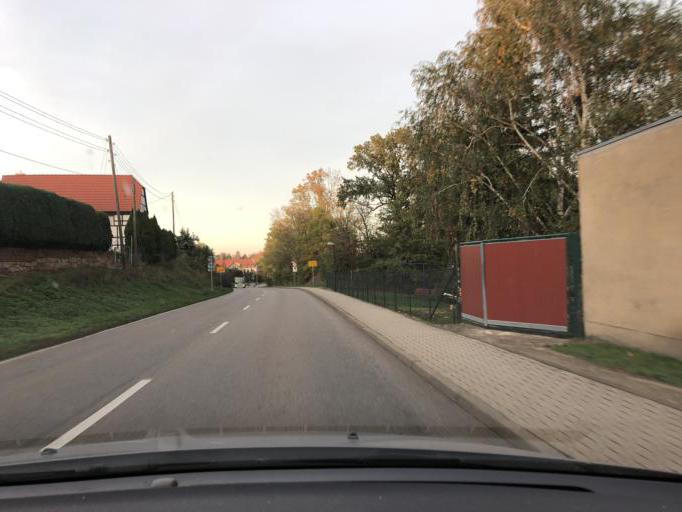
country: DE
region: Saxony
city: Elstertrebnitz
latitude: 51.1126
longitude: 12.1949
